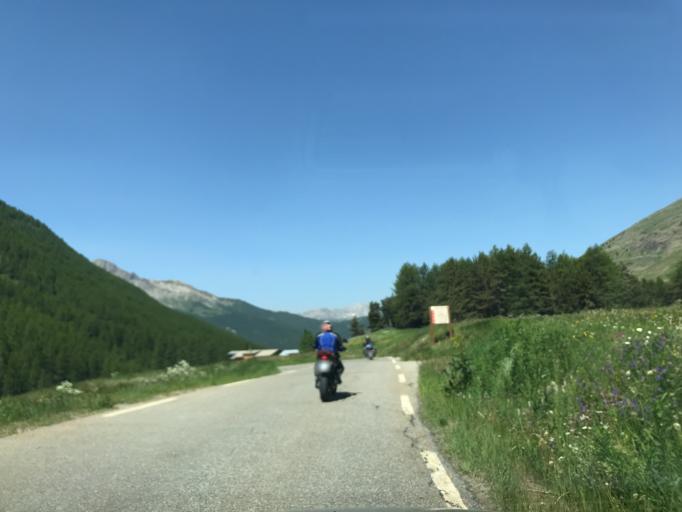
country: IT
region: Piedmont
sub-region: Provincia di Cuneo
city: Pontechianale
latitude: 44.7210
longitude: 6.8917
